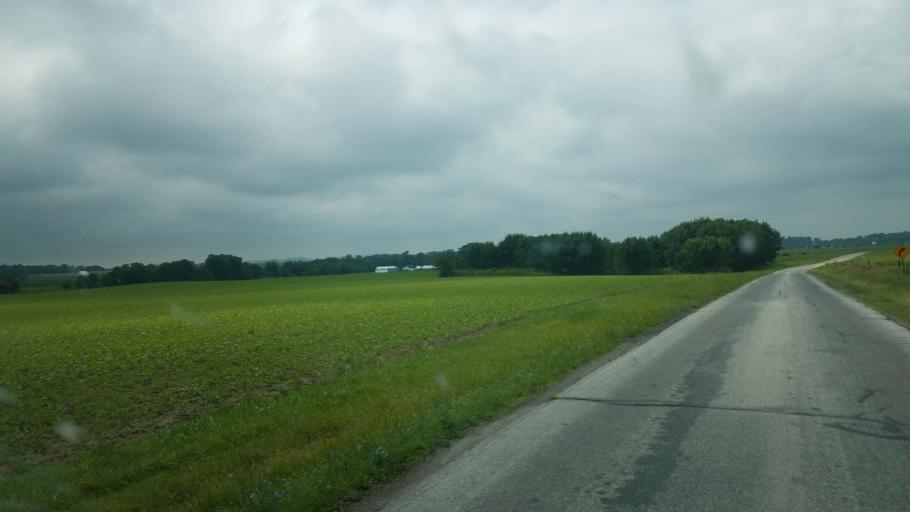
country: US
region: Ohio
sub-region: Highland County
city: Leesburg
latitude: 39.2402
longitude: -83.4876
